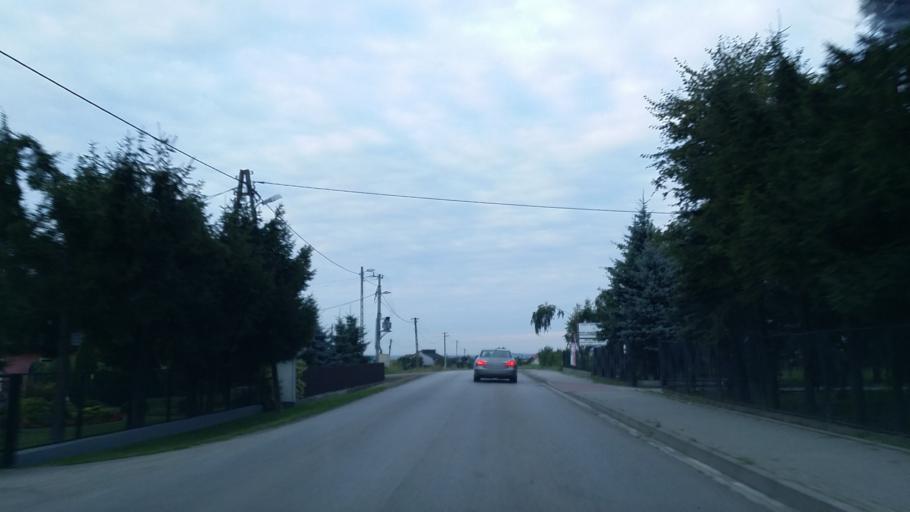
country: PL
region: Lesser Poland Voivodeship
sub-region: Powiat krakowski
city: Kaszow
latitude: 50.0204
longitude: 19.7258
